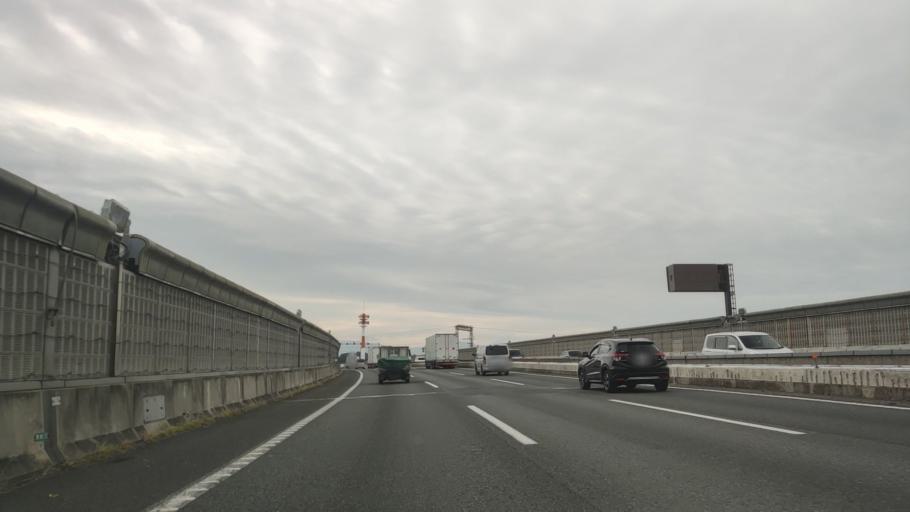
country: JP
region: Osaka
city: Kashihara
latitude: 34.5721
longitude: 135.6039
